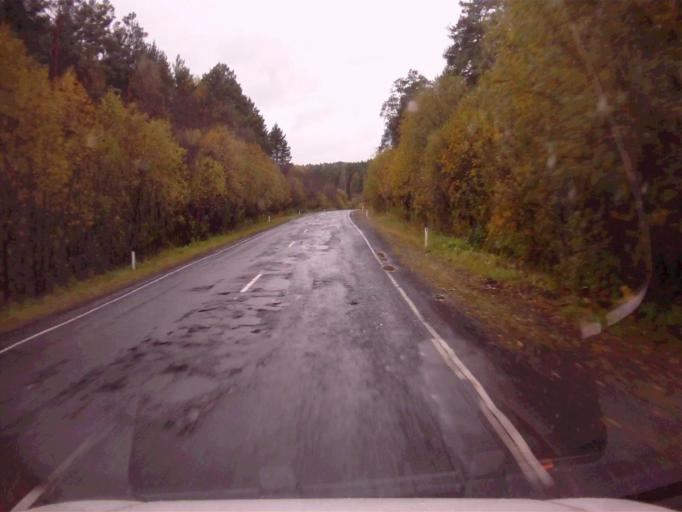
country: RU
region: Chelyabinsk
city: Verkhniy Ufaley
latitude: 56.0493
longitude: 60.1407
